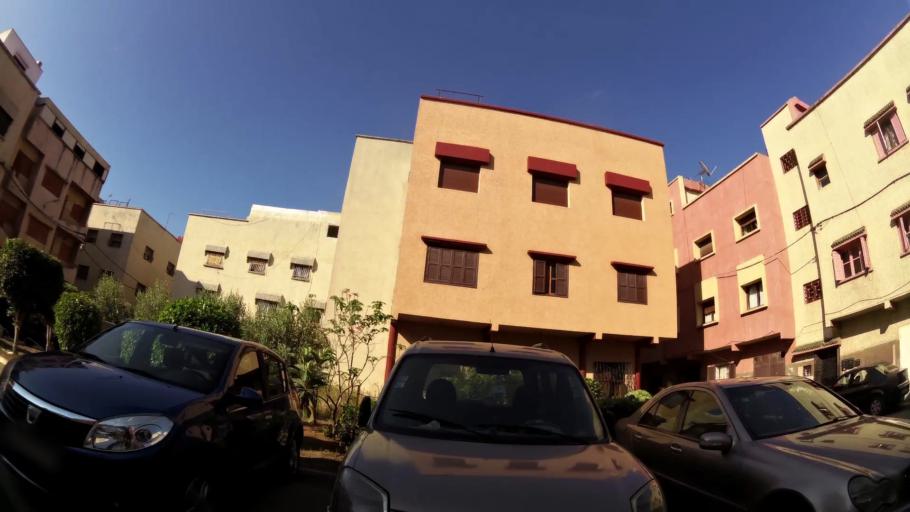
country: MA
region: Rabat-Sale-Zemmour-Zaer
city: Sale
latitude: 34.0455
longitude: -6.8133
